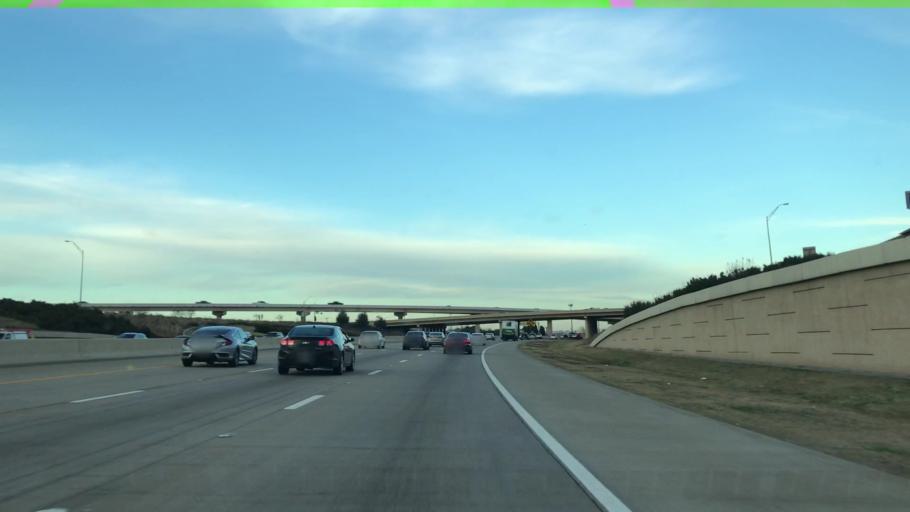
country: US
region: Texas
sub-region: Denton County
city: The Colony
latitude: 33.0487
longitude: -96.9215
